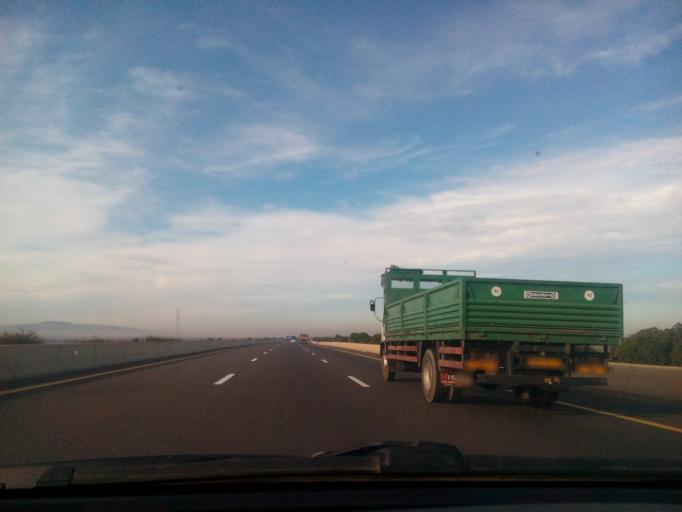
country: DZ
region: Mascara
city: Sig
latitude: 35.5883
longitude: -0.0872
